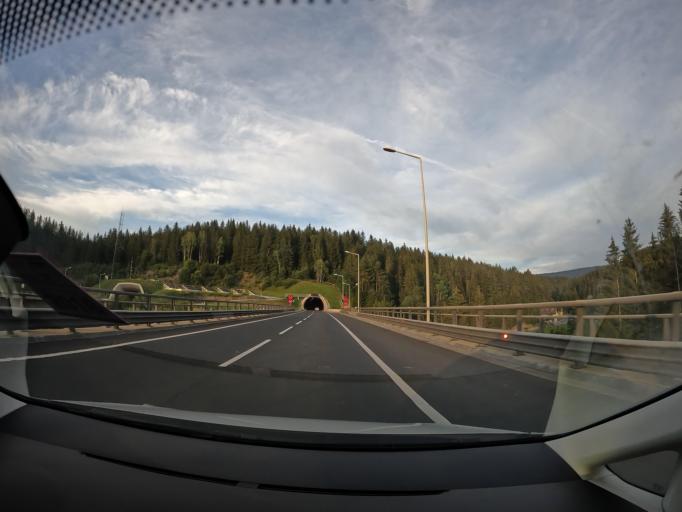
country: AT
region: Styria
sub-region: Politischer Bezirk Voitsberg
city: Modriach
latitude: 46.9586
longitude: 15.0588
